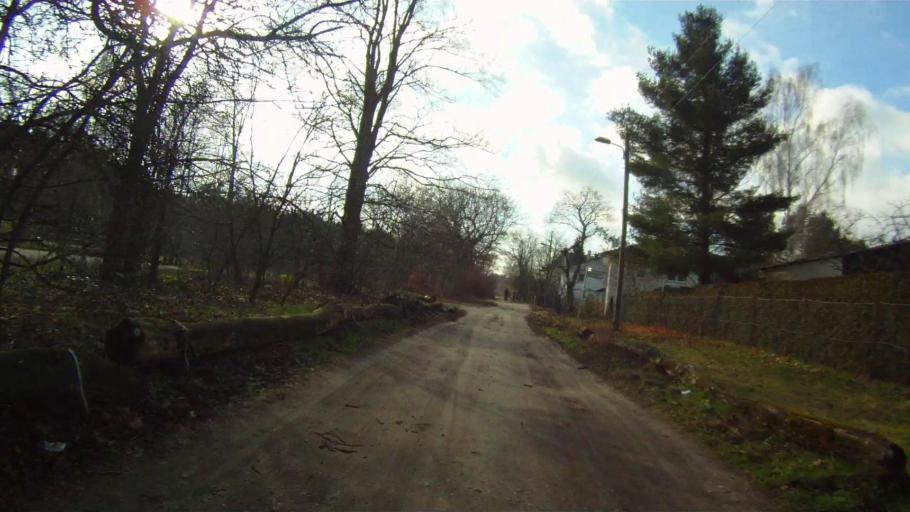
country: DE
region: Berlin
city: Friedrichshagen
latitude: 52.4735
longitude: 13.6150
